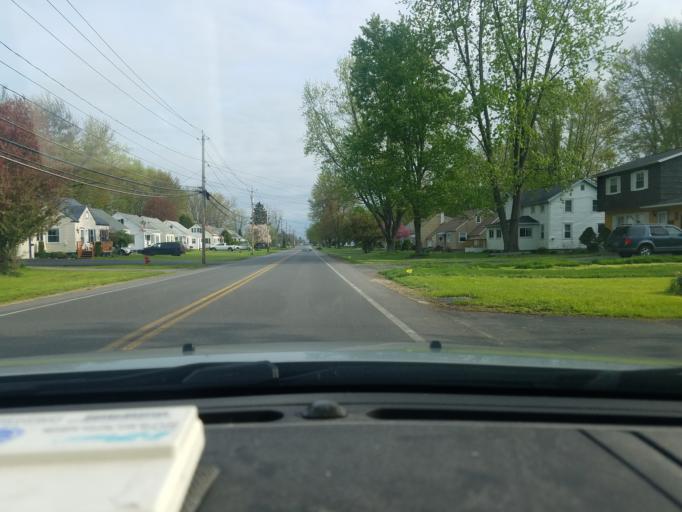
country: US
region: New York
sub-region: Onondaga County
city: East Syracuse
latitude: 43.0778
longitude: -76.0775
